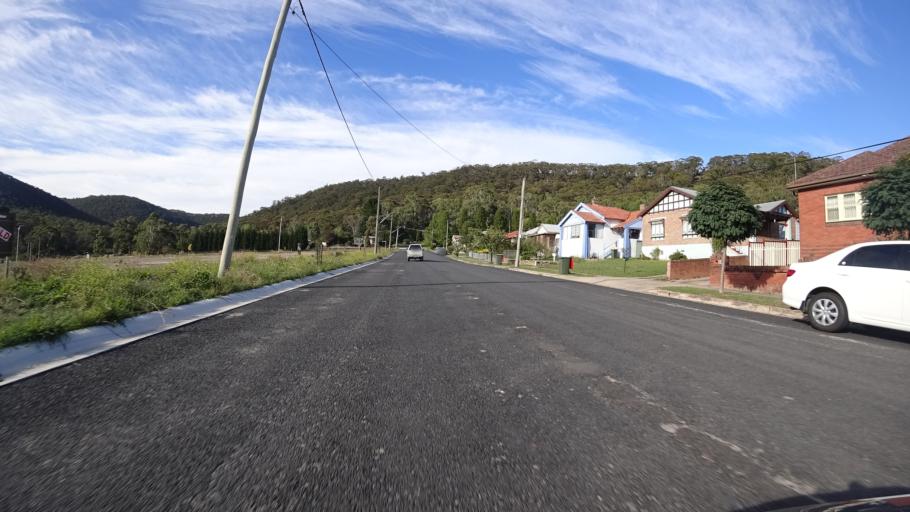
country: AU
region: New South Wales
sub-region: Lithgow
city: Lithgow
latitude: -33.4920
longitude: 150.1504
